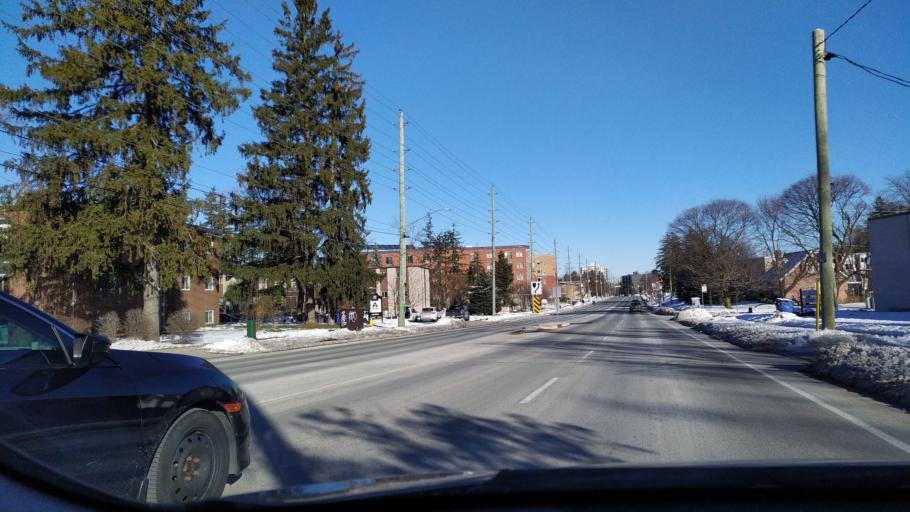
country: CA
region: Ontario
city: Waterloo
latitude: 43.4538
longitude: -80.5498
